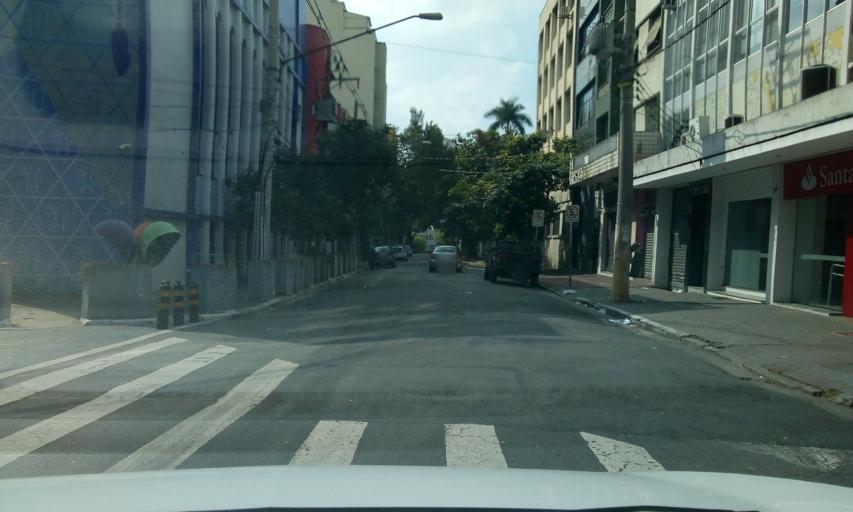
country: BR
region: Sao Paulo
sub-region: Sao Paulo
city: Sao Paulo
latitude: -23.5302
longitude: -46.6385
